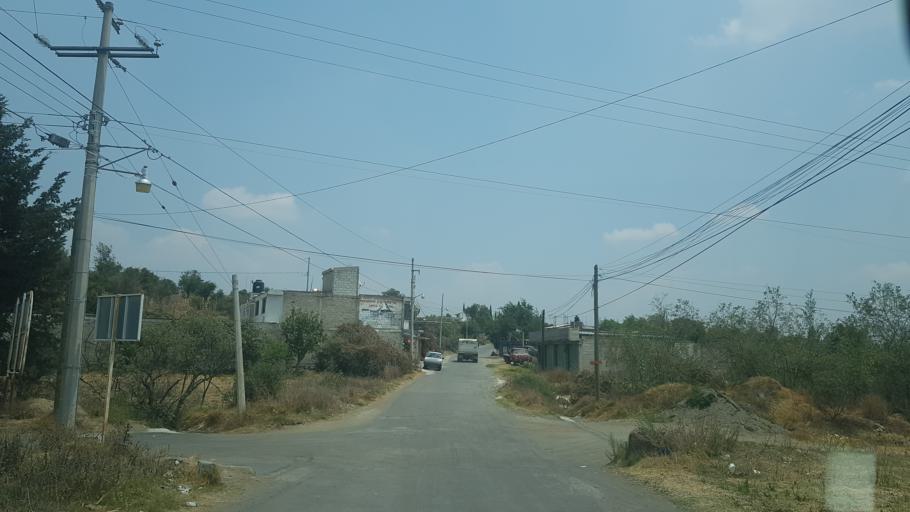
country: MX
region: Puebla
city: San Andres Calpan
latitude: 19.0998
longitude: -98.4756
